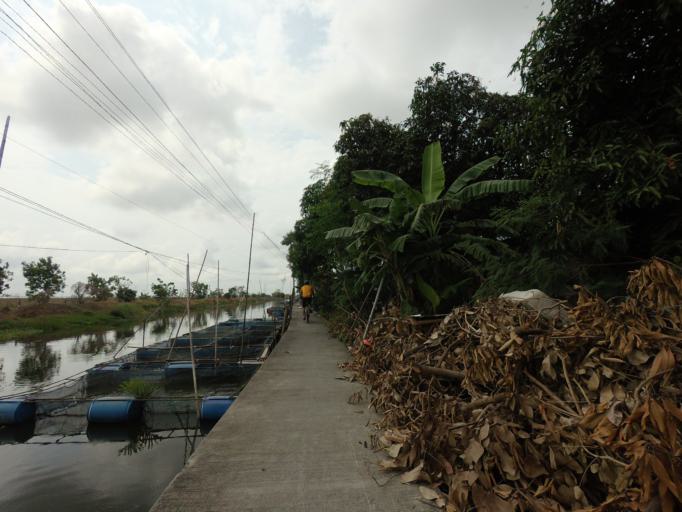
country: TH
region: Bangkok
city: Lat Krabang
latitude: 13.6869
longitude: 100.7315
